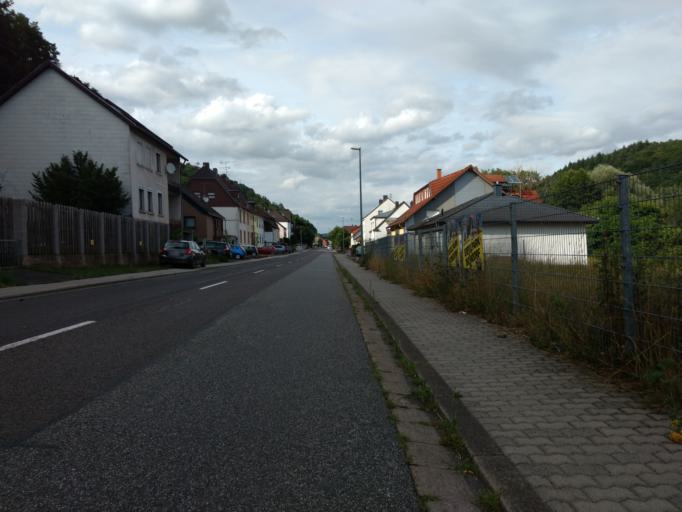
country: DE
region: Saarland
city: Beckingen
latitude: 49.4038
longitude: 6.7125
